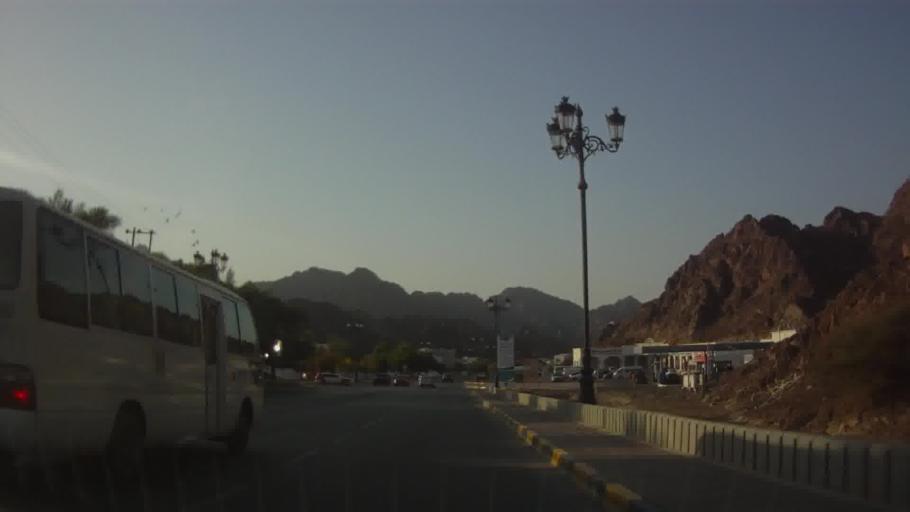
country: OM
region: Muhafazat Masqat
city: Muscat
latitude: 23.5892
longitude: 58.6000
